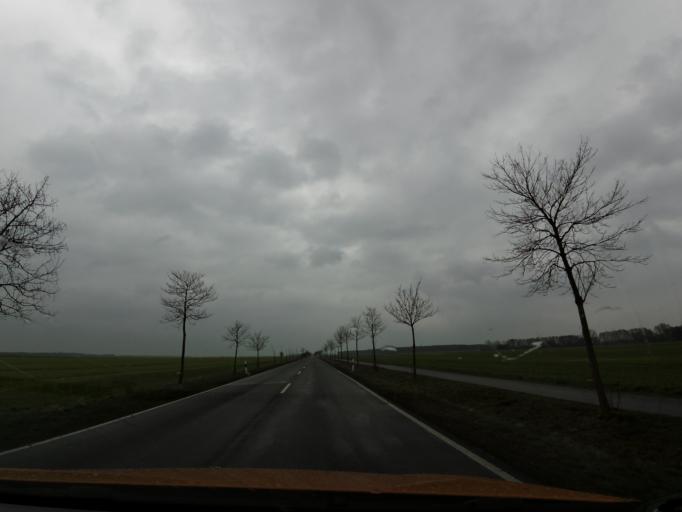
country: DE
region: Brandenburg
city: Ziesar
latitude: 52.2781
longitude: 12.2416
